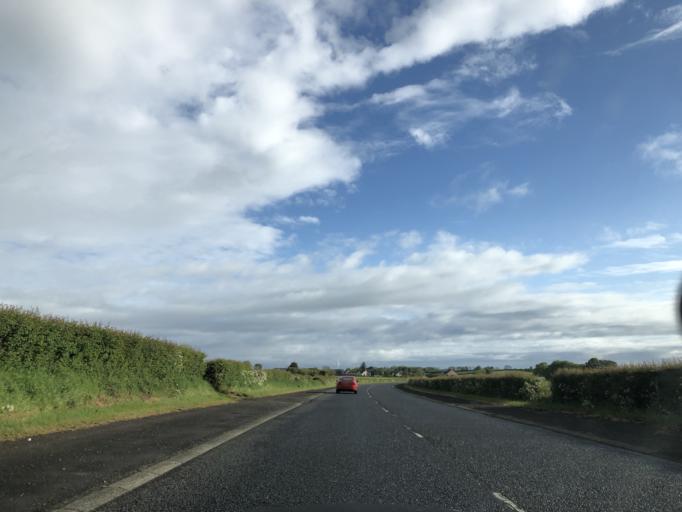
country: GB
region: Northern Ireland
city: Bushmills
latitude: 55.1593
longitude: -6.5753
